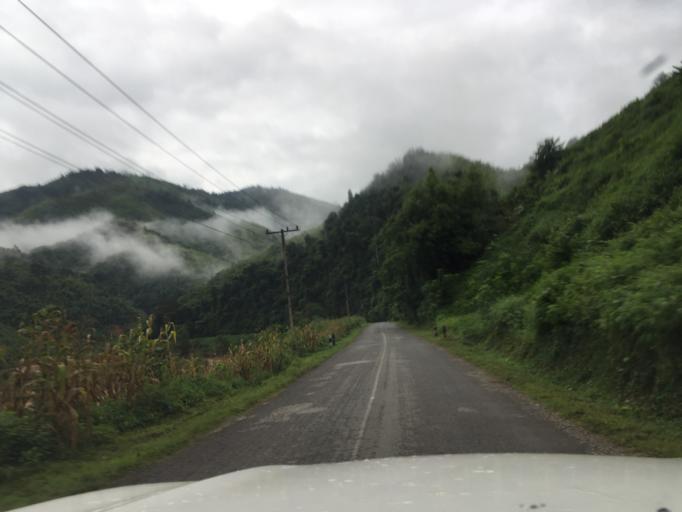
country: LA
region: Oudomxai
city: Muang La
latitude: 20.9240
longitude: 102.2024
